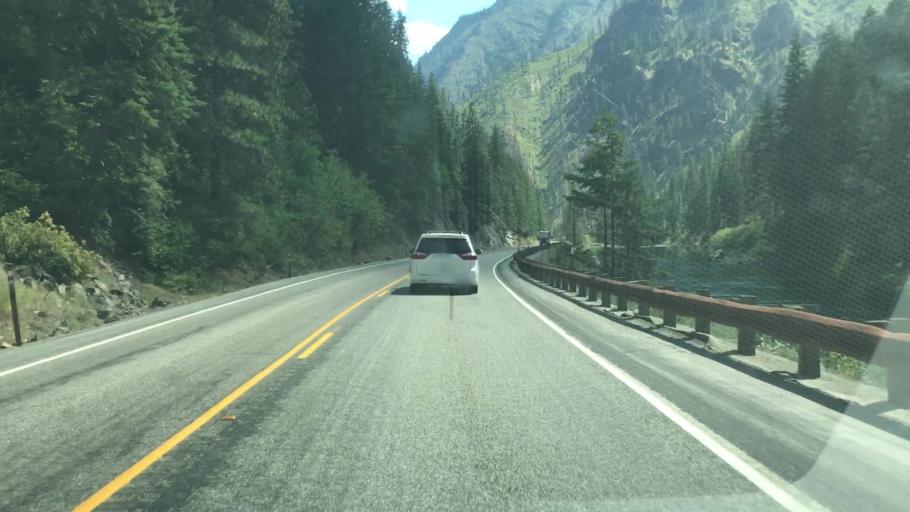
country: US
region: Washington
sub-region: Chelan County
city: Leavenworth
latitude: 47.6729
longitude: -120.7350
